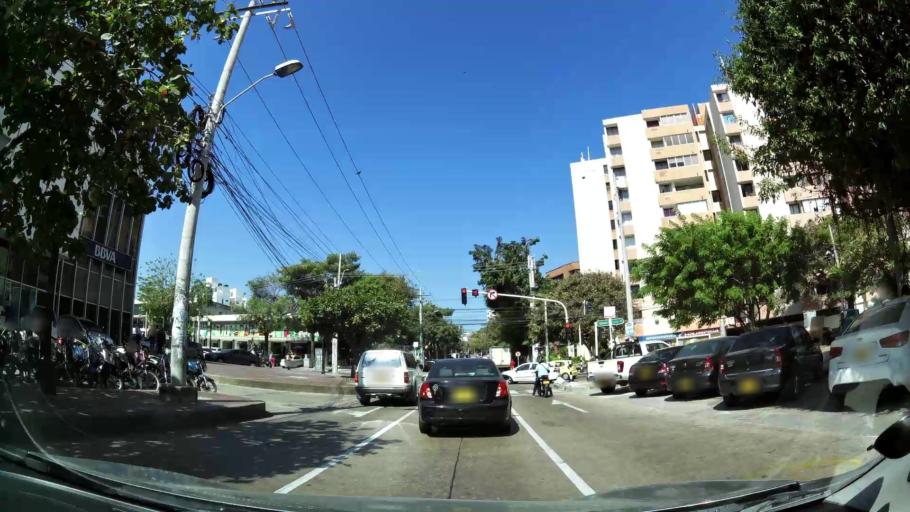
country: CO
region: Atlantico
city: Barranquilla
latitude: 10.9971
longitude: -74.8004
